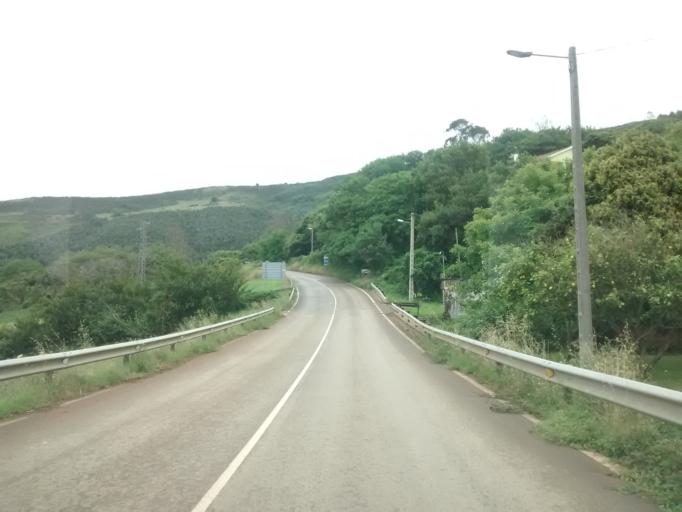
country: ES
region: Cantabria
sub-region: Provincia de Cantabria
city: Santillana
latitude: 43.4119
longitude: -4.1023
